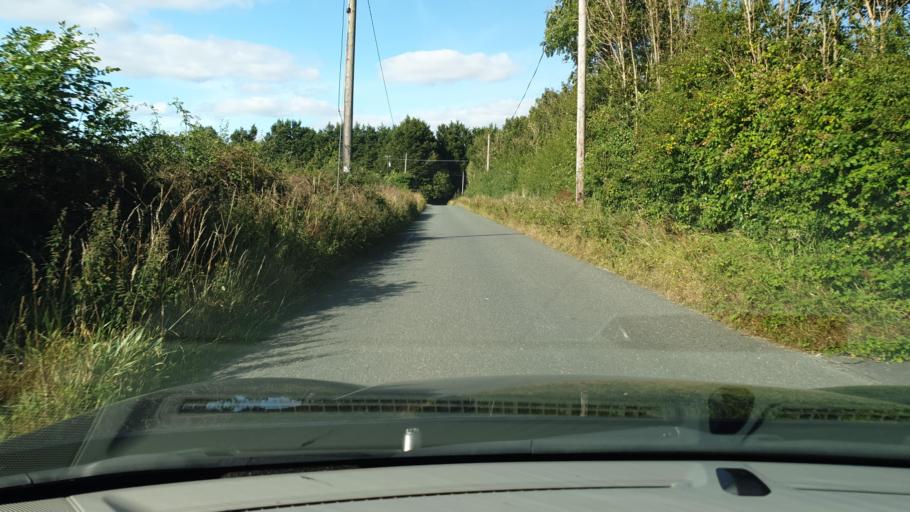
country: IE
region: Leinster
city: Hartstown
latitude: 53.4245
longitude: -6.4305
